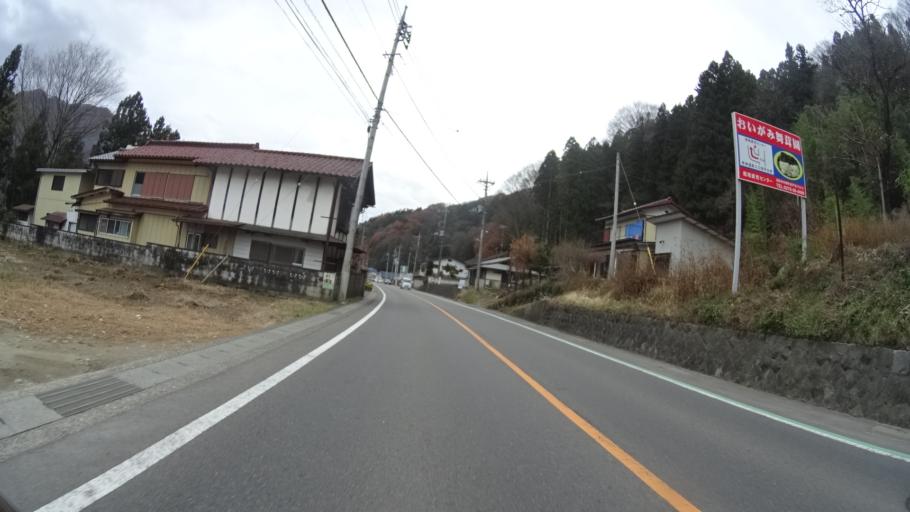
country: JP
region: Gunma
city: Numata
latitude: 36.6908
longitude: 139.2079
